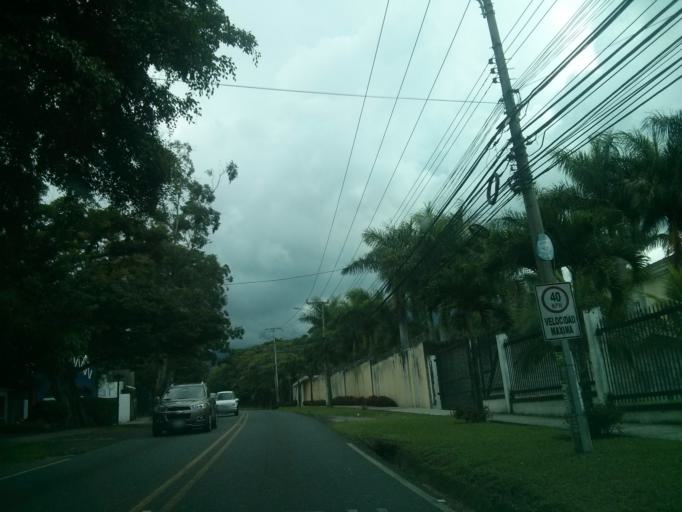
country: CR
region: San Jose
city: San Rafael
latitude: 9.9356
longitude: -84.1516
